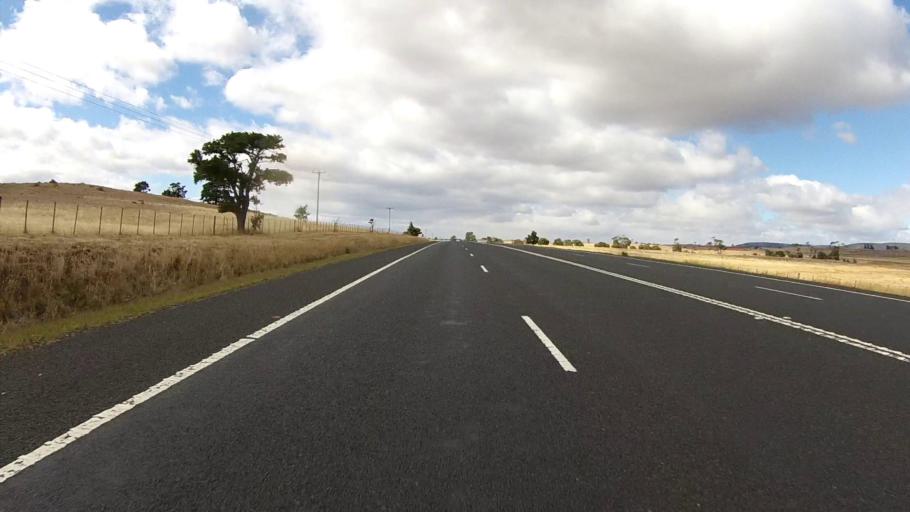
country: AU
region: Tasmania
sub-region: Northern Midlands
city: Evandale
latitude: -41.8683
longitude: 147.4591
